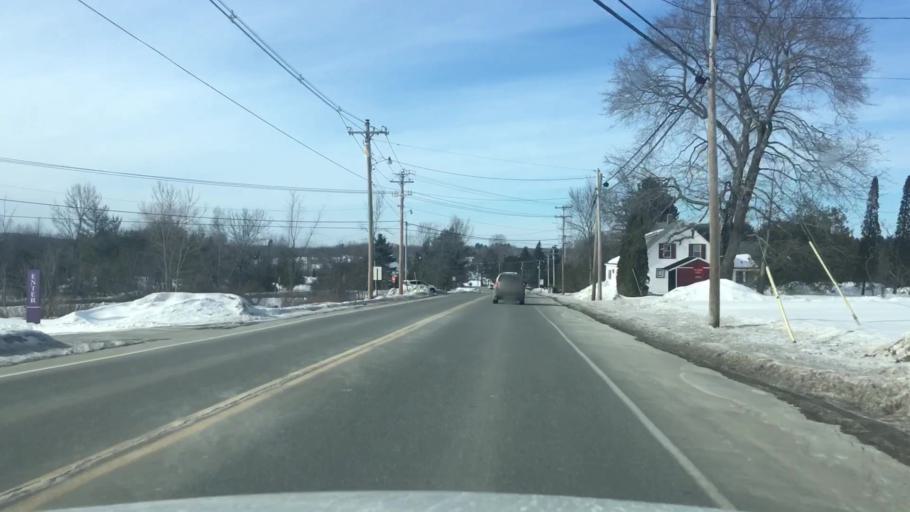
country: US
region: Maine
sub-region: Penobscot County
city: Bangor
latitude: 44.8491
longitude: -68.8038
